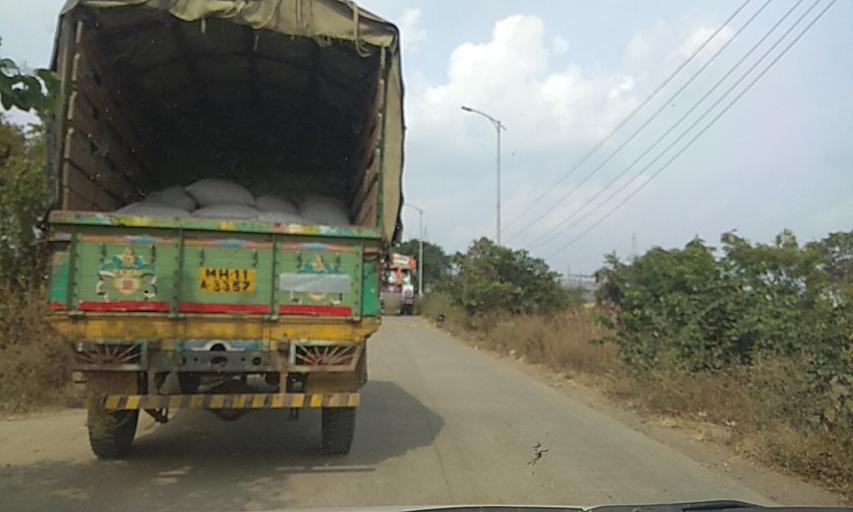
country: IN
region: Maharashtra
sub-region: Pune Division
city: Pimpri
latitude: 18.5855
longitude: 73.7059
